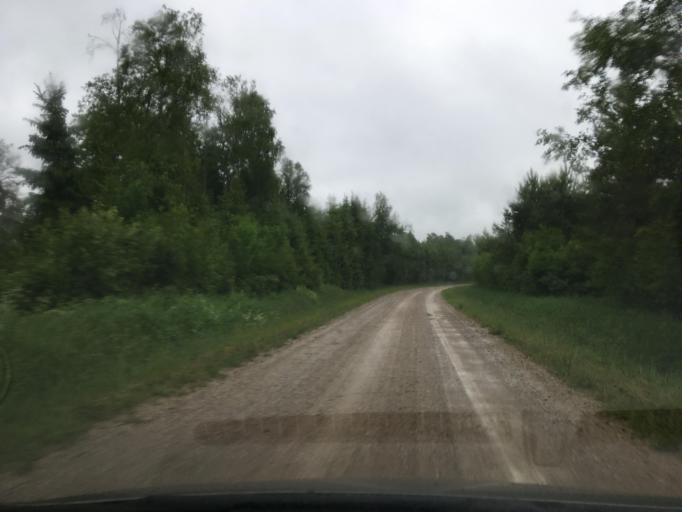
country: EE
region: Laeaene
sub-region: Lihula vald
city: Lihula
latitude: 58.6324
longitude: 23.8054
